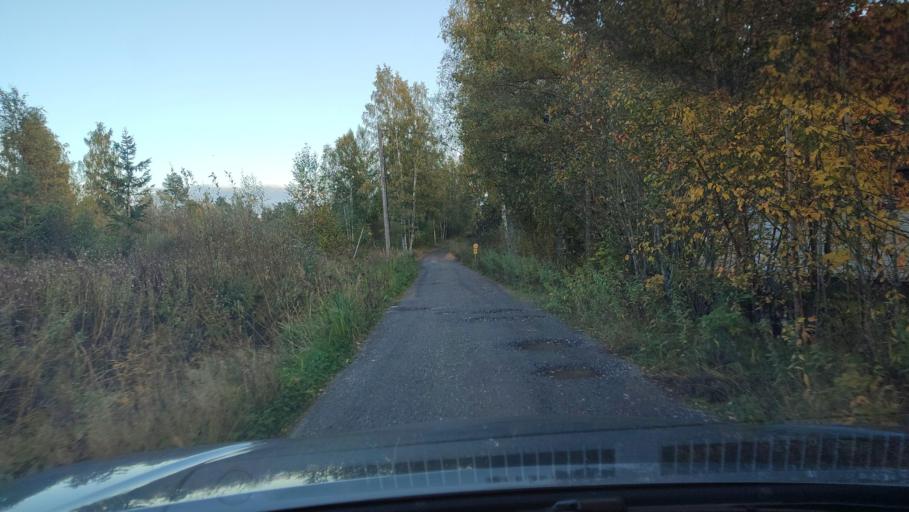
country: FI
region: Ostrobothnia
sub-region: Sydosterbotten
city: Kristinestad
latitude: 62.2423
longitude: 21.5139
